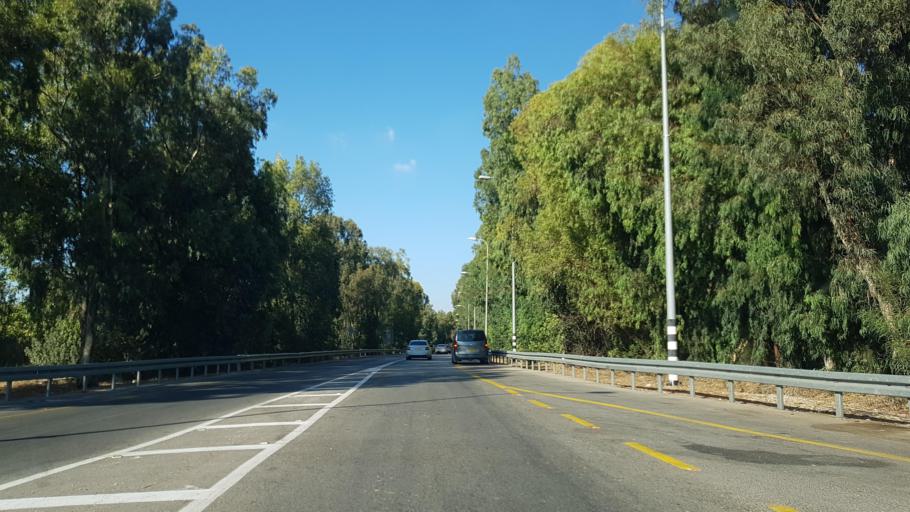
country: PS
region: West Bank
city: Tulkarm
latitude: 32.3515
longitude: 35.0138
